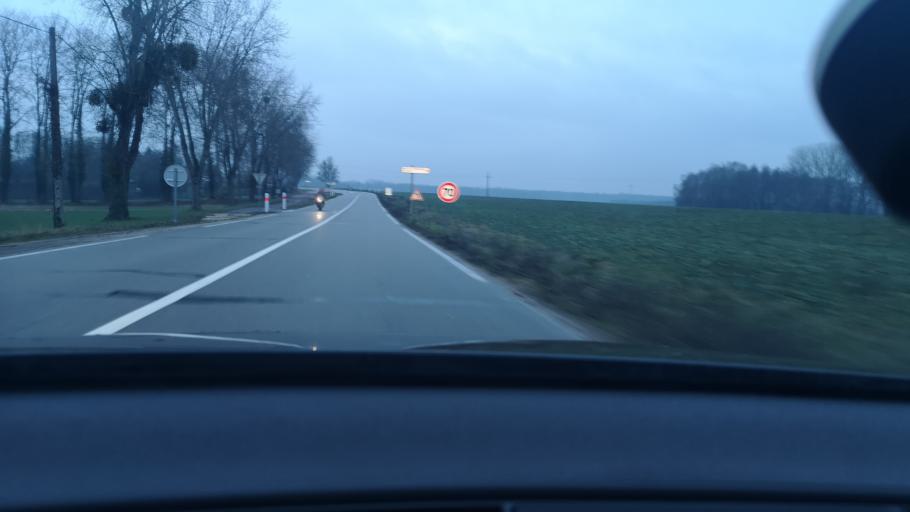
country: FR
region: Bourgogne
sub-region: Departement de la Cote-d'Or
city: Seurre
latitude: 47.0619
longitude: 5.0944
